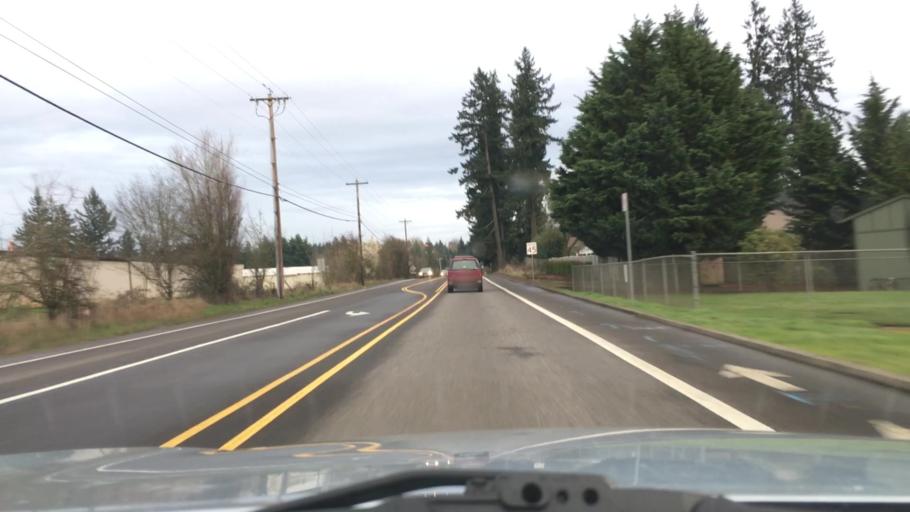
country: US
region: Oregon
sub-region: Clackamas County
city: Beavercreek
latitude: 45.3169
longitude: -122.5545
